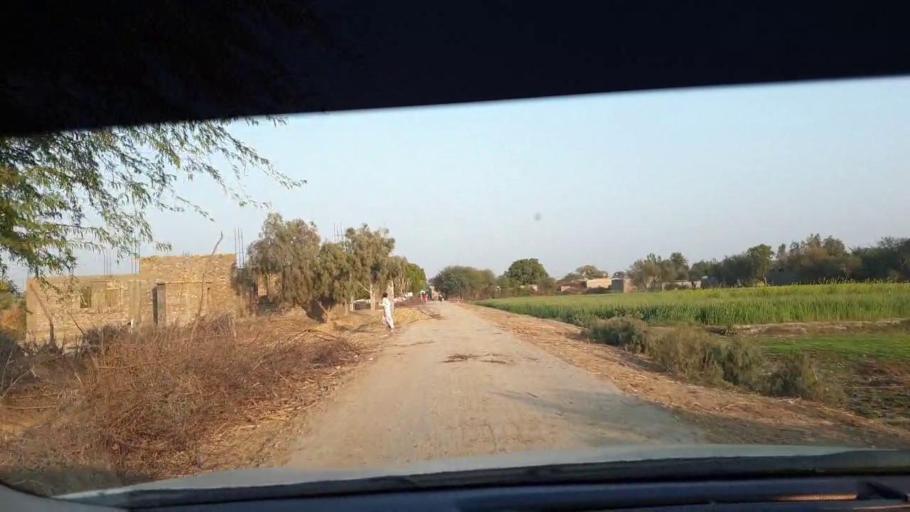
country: PK
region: Sindh
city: Berani
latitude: 25.8522
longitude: 68.8169
